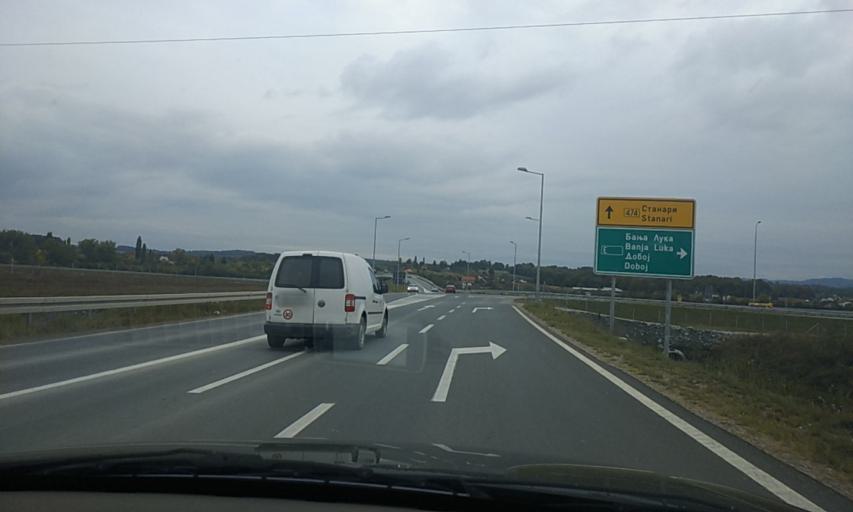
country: BA
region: Republika Srpska
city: Prnjavor
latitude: 44.8547
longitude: 17.6893
